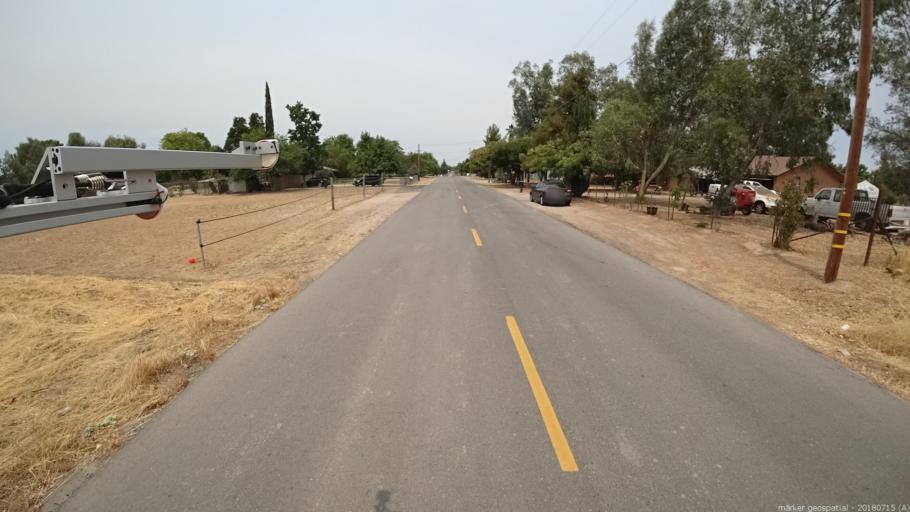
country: US
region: California
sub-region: Madera County
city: Madera Acres
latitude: 37.0016
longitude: -120.0847
